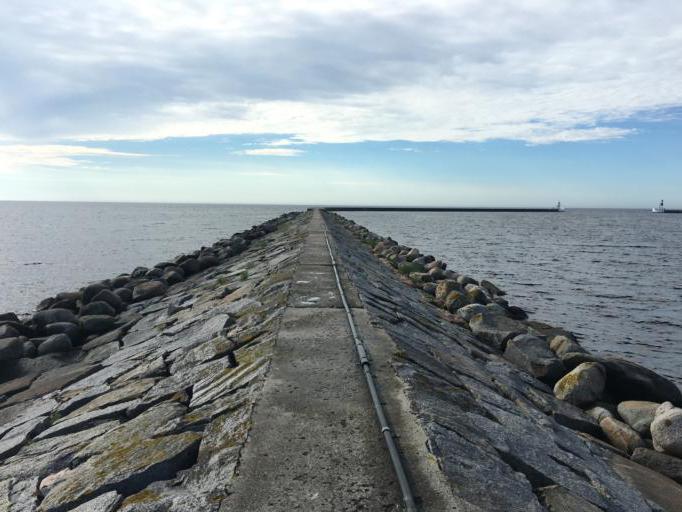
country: SE
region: Skane
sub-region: Vellinge Kommun
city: Hollviken
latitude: 55.3974
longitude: 12.9493
